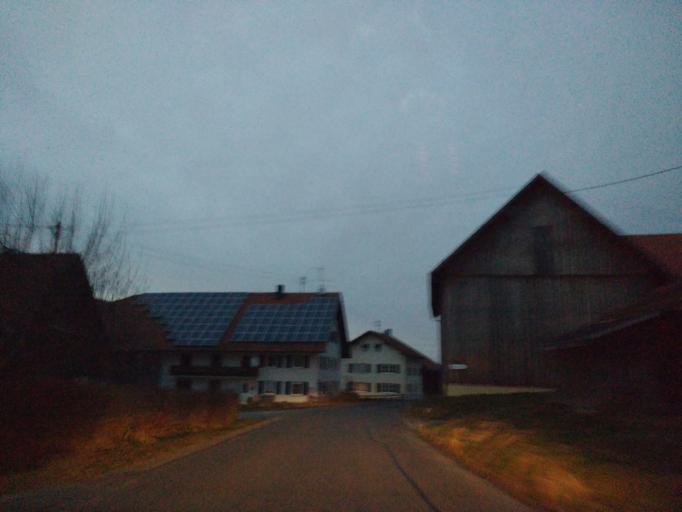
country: DE
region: Bavaria
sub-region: Swabia
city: Bidingen
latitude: 47.8217
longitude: 10.7300
